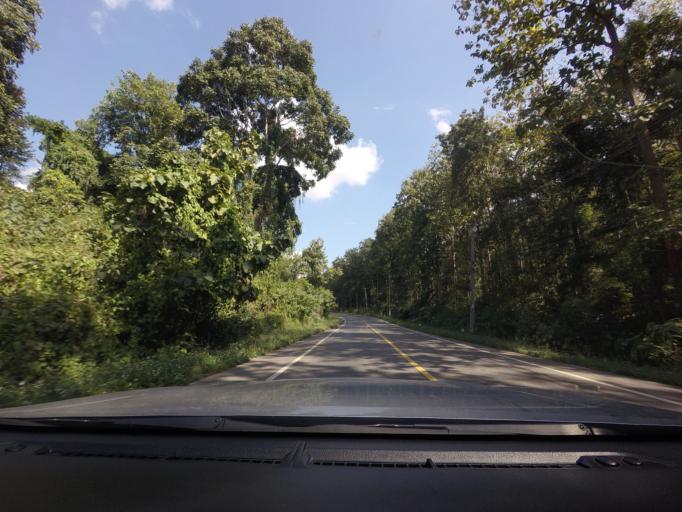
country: TH
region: Chiang Mai
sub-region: Amphoe Chiang Dao
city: Chiang Dao
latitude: 19.4726
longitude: 99.0044
